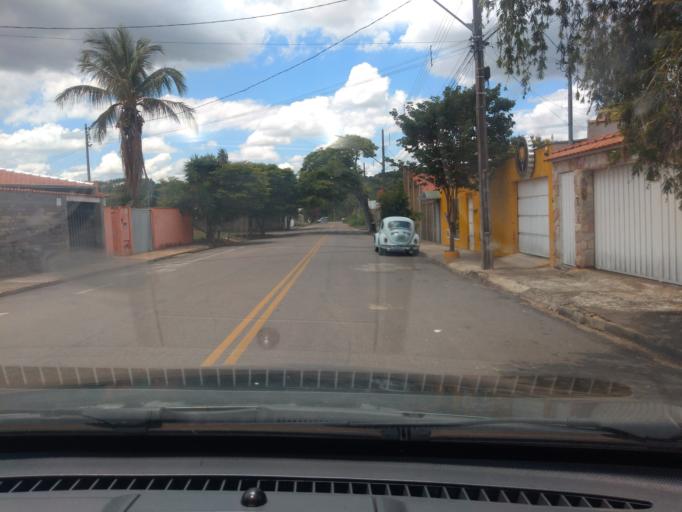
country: BR
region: Minas Gerais
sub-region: Tres Coracoes
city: Tres Coracoes
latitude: -21.6751
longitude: -45.2659
